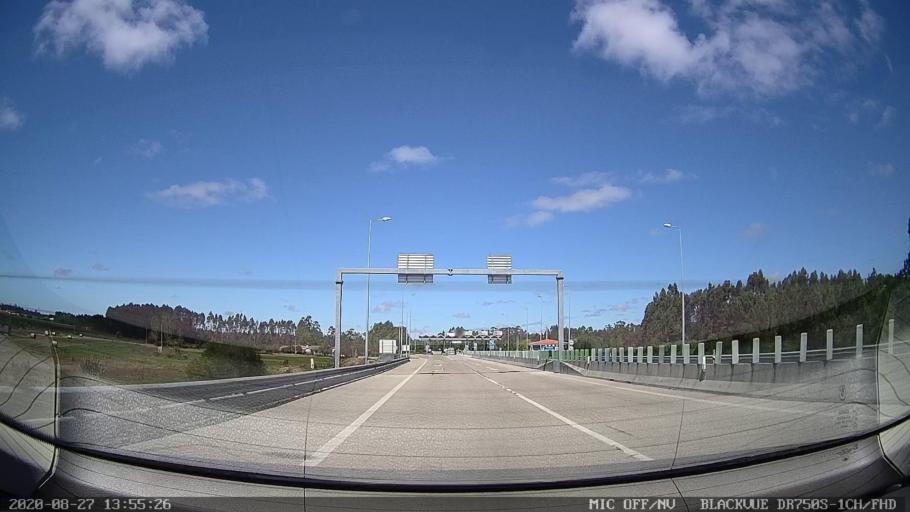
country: PT
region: Coimbra
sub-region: Montemor-O-Velho
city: Arazede
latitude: 40.3279
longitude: -8.7248
